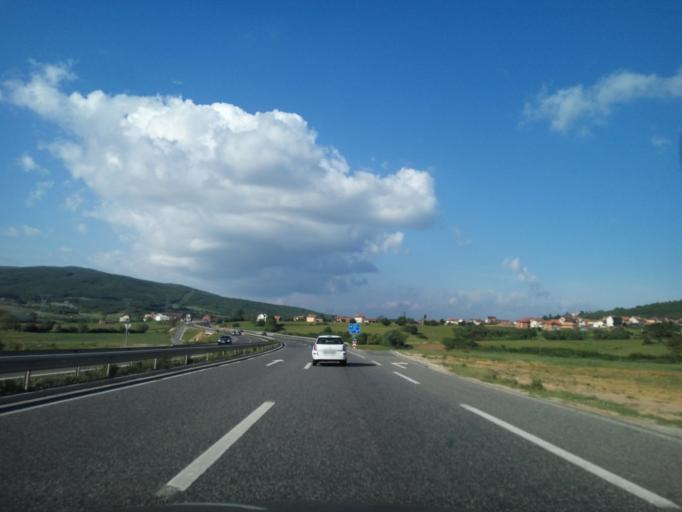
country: XK
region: Prizren
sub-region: Komuna e Malisheves
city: Llazice
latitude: 42.5598
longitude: 20.8246
